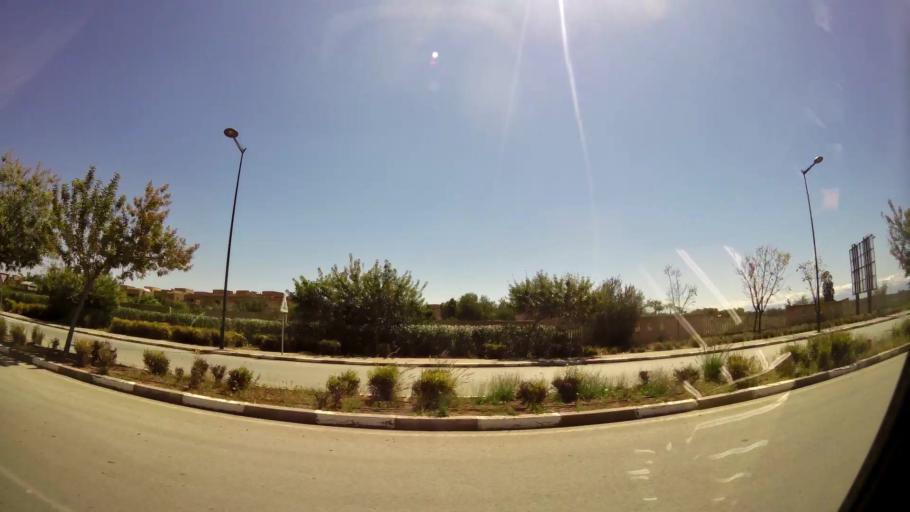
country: MA
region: Marrakech-Tensift-Al Haouz
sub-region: Marrakech
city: Marrakesh
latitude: 31.5991
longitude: -8.0059
